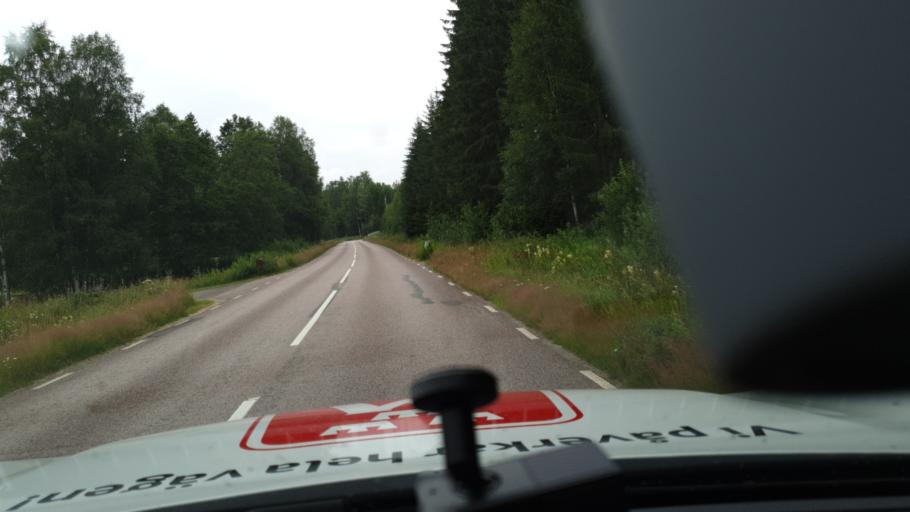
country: SE
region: Vaermland
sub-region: Sunne Kommun
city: Sunne
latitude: 59.7689
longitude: 13.2383
